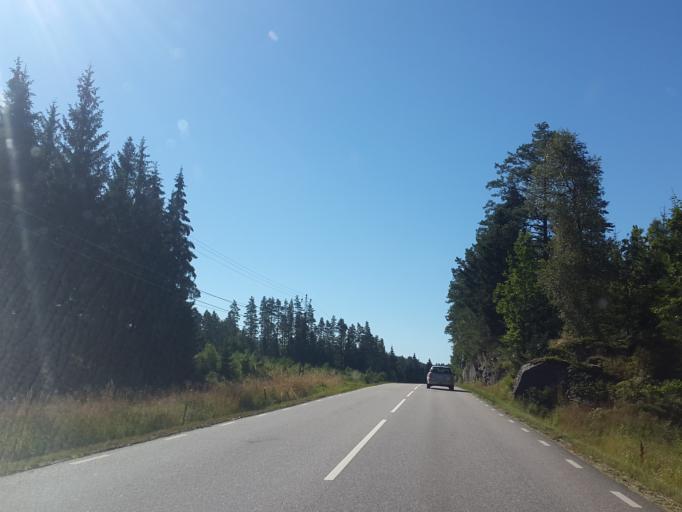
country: SE
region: Vaestra Goetaland
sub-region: Herrljunga Kommun
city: Herrljunga
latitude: 57.9249
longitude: 13.0255
